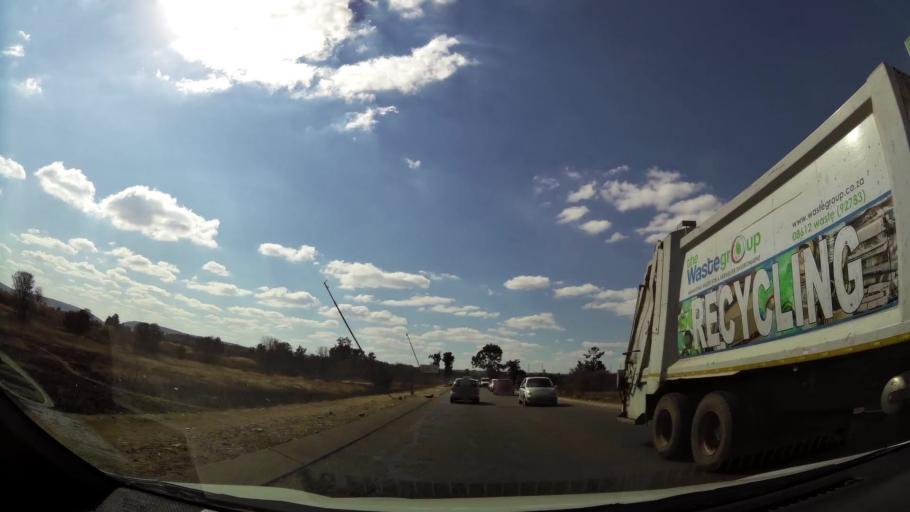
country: ZA
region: Gauteng
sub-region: City of Tshwane Metropolitan Municipality
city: Cullinan
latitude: -25.7481
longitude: 28.3708
